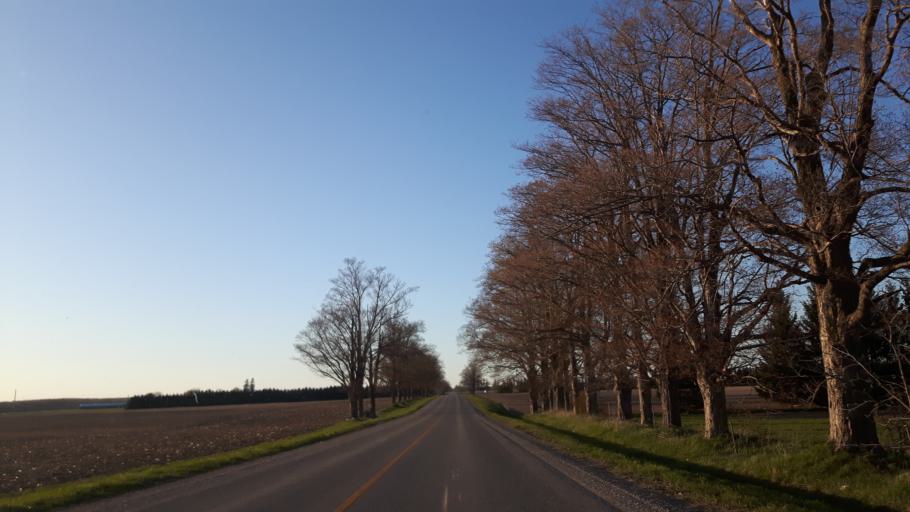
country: CA
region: Ontario
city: Bluewater
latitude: 43.5440
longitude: -81.5468
